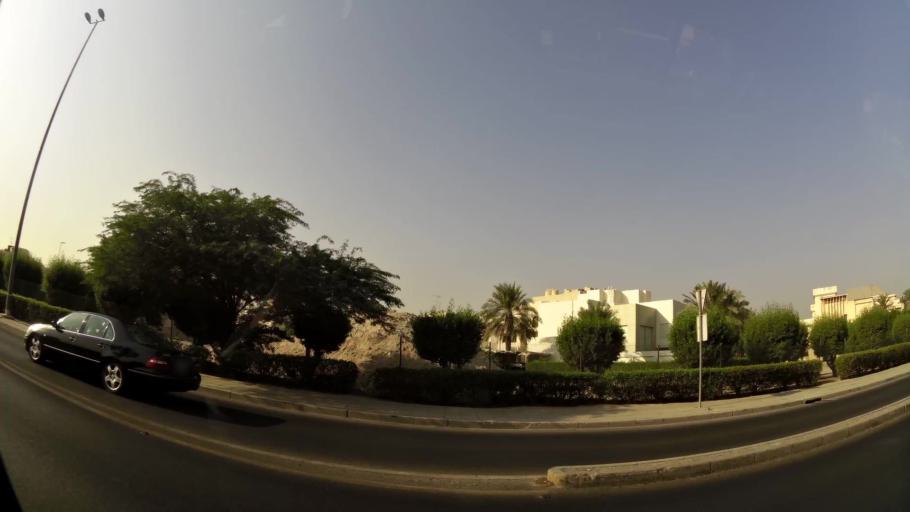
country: KW
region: Al Asimah
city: Ad Dasmah
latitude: 29.3620
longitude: 48.0165
